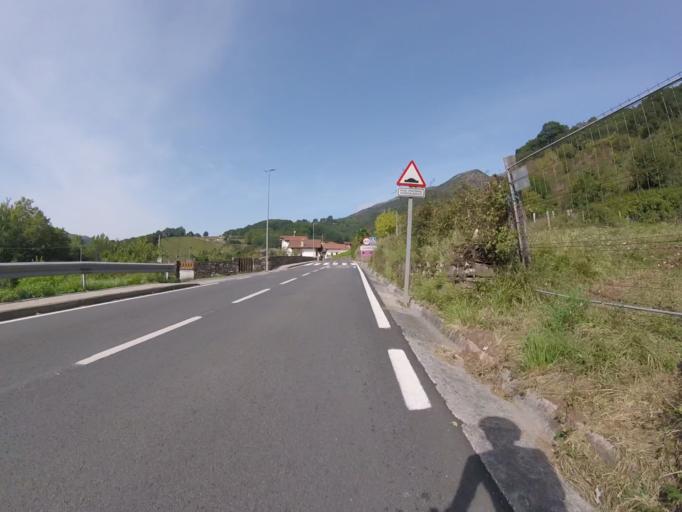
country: ES
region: Navarre
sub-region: Provincia de Navarra
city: Elgorriaga
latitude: 43.1387
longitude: -1.6839
